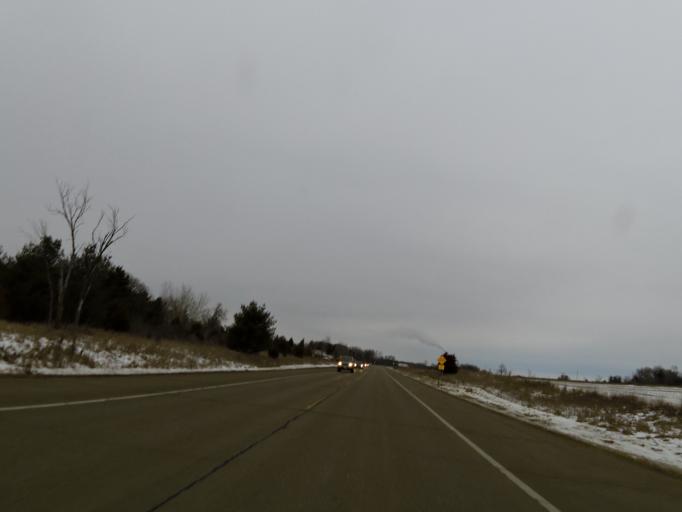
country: US
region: Wisconsin
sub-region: Saint Croix County
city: Hudson
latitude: 44.9825
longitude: -92.7782
